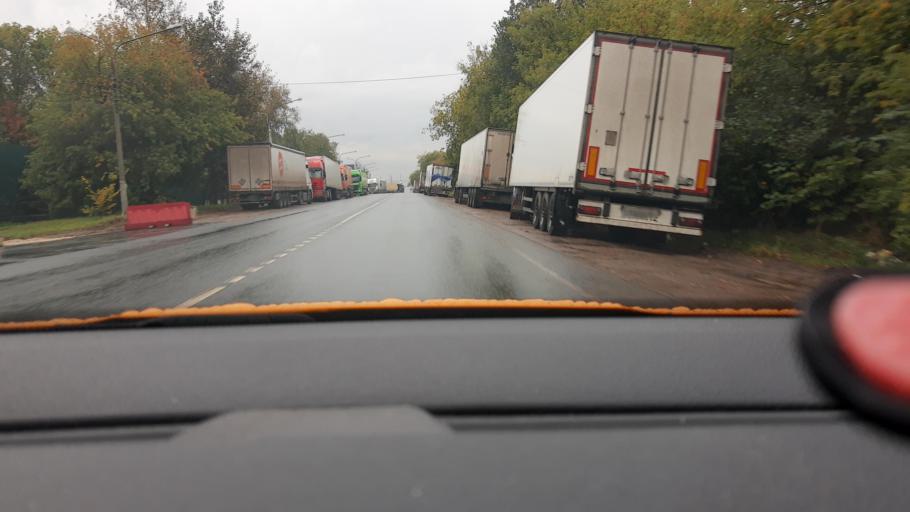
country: RU
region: Moskovskaya
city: Obukhovo
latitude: 55.8228
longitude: 38.2617
